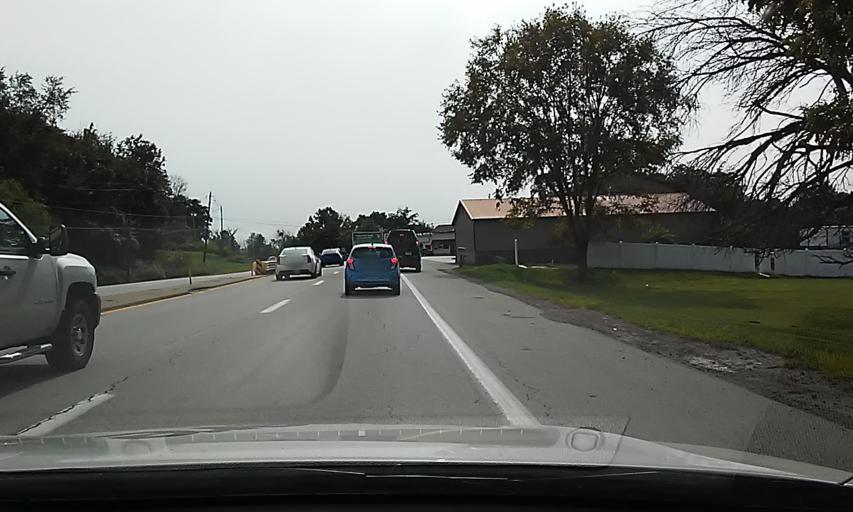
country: US
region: Pennsylvania
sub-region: Fayette County
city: Connellsville
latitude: 40.0359
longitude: -79.5845
